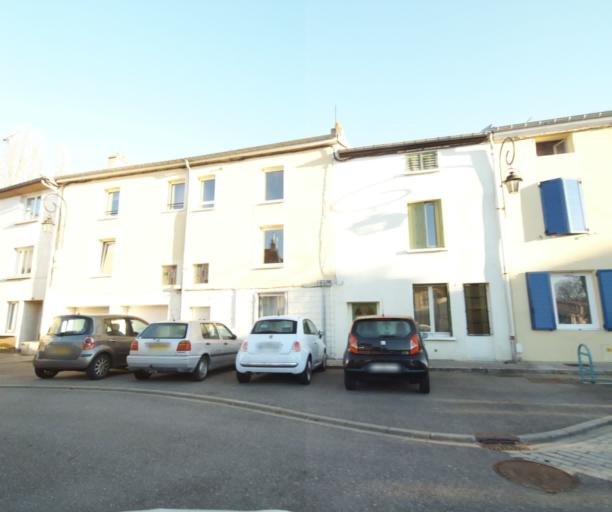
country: FR
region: Lorraine
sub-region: Departement de Meurthe-et-Moselle
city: Laxou
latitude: 48.6864
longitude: 6.1405
